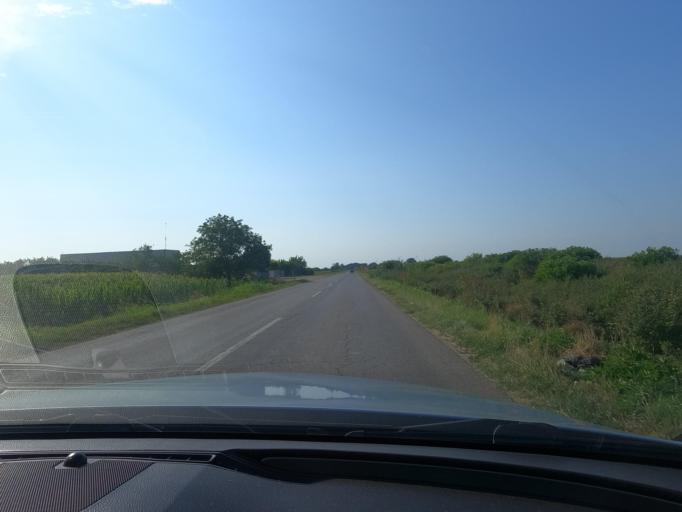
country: RS
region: Autonomna Pokrajina Vojvodina
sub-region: Juznobacki Okrug
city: Kovilj
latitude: 45.2866
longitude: 19.9685
